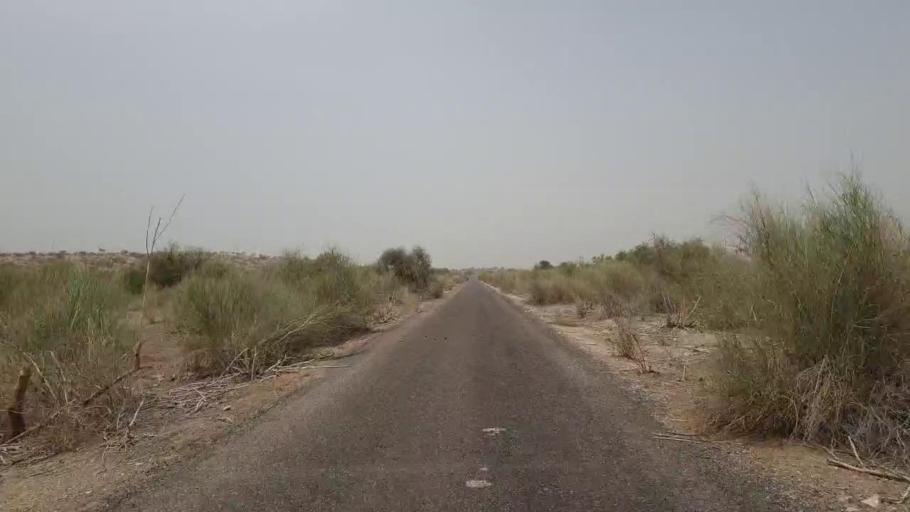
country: PK
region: Sindh
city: Islamkot
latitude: 24.7770
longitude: 70.4954
